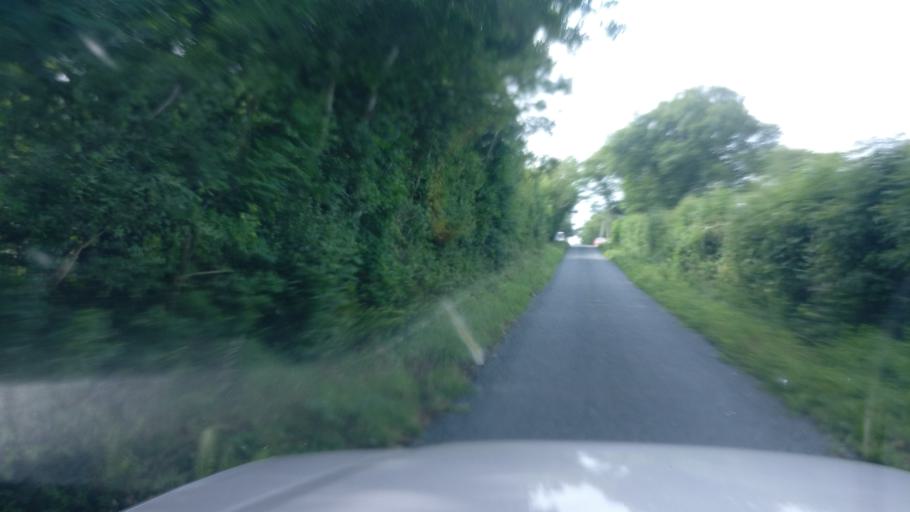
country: IE
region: Connaught
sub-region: County Galway
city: Gort
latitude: 53.1069
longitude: -8.7149
